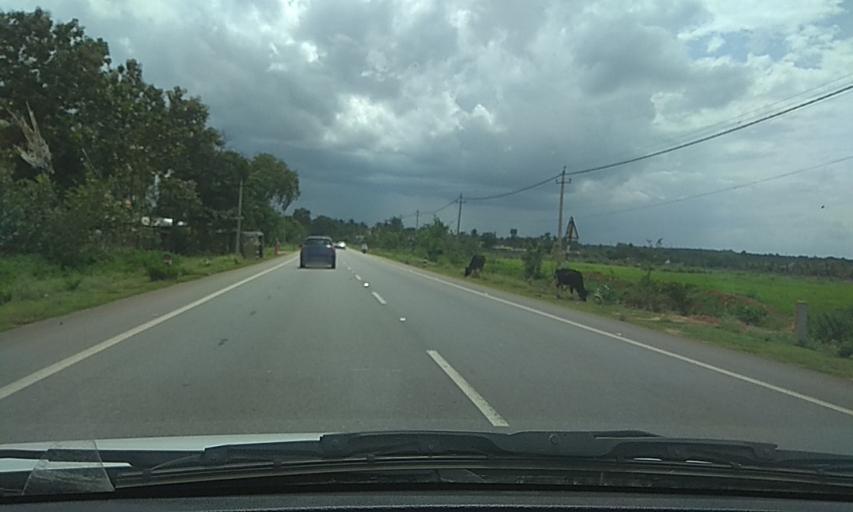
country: IN
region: Karnataka
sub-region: Tumkur
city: Tumkur
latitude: 13.2308
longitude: 77.0686
